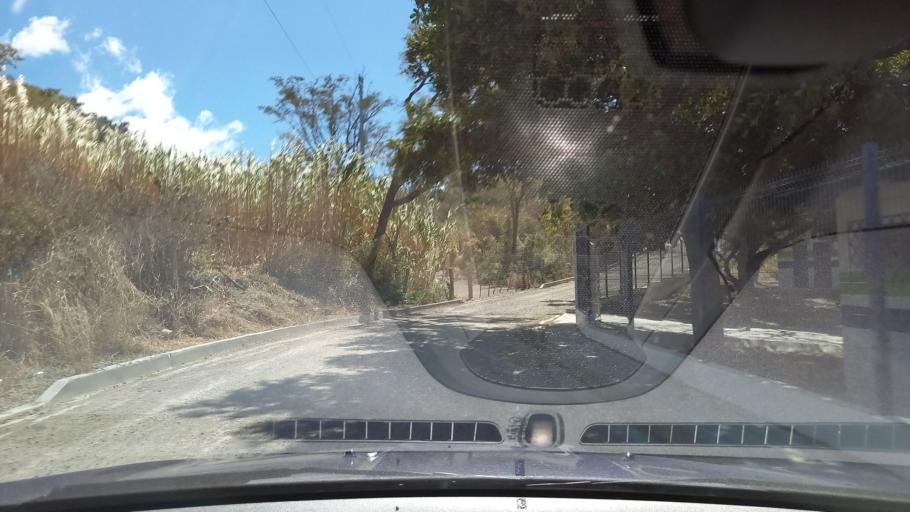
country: SV
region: Santa Ana
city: Metapan
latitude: 14.3705
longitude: -89.4865
